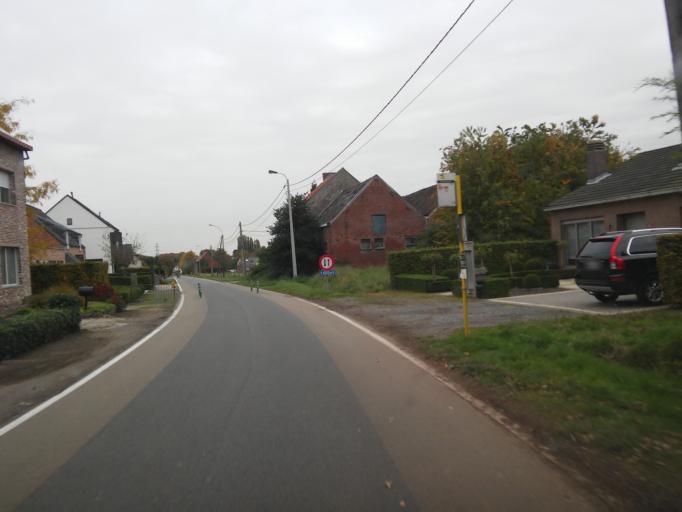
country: BE
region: Flanders
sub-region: Provincie Antwerpen
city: Rumst
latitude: 51.0953
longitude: 4.4001
